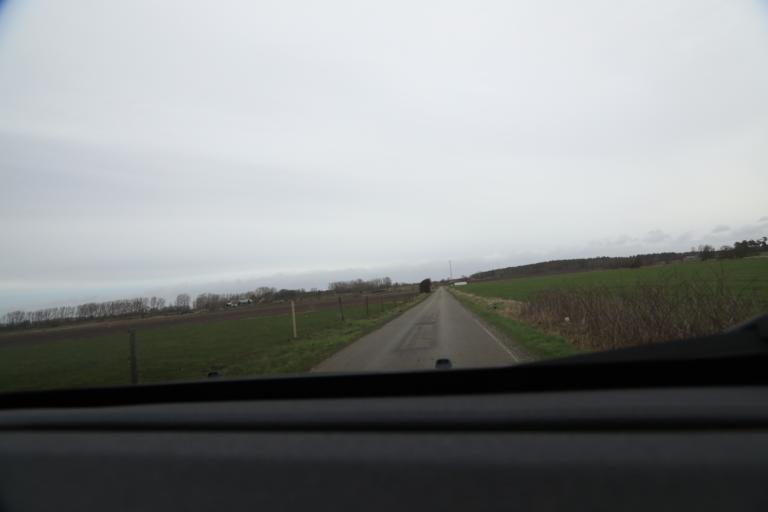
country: SE
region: Halland
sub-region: Varbergs Kommun
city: Traslovslage
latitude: 57.0737
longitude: 12.2983
